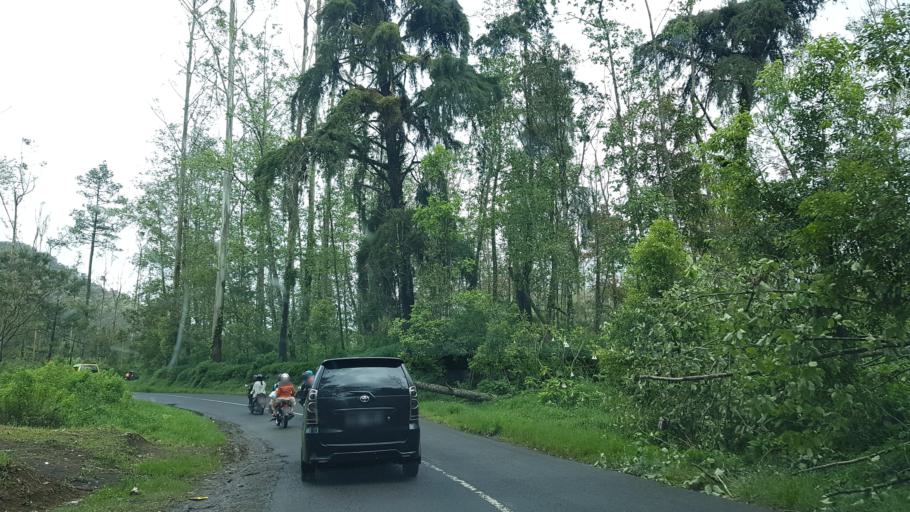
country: ID
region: West Java
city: Banjar
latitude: -7.1424
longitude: 107.3932
